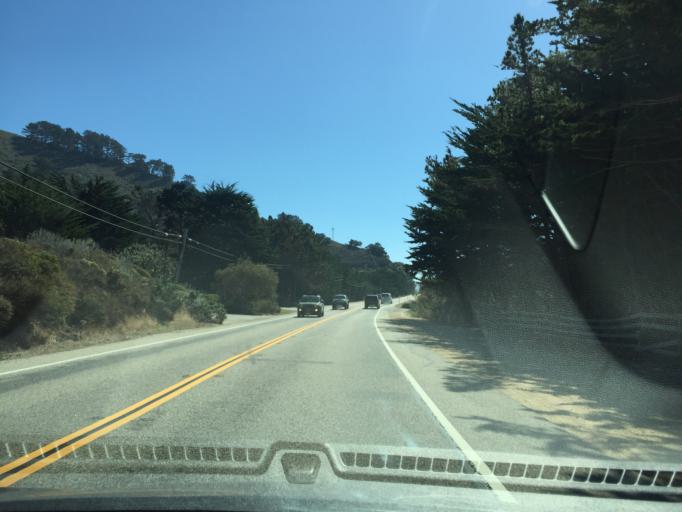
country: US
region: California
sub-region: Monterey County
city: Carmel-by-the-Sea
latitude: 36.4069
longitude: -121.9114
